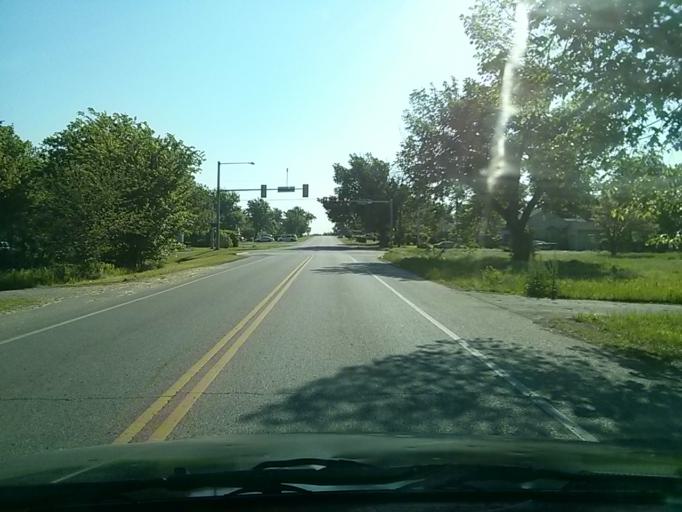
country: US
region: Oklahoma
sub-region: Tulsa County
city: Tulsa
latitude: 36.1929
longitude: -95.9876
